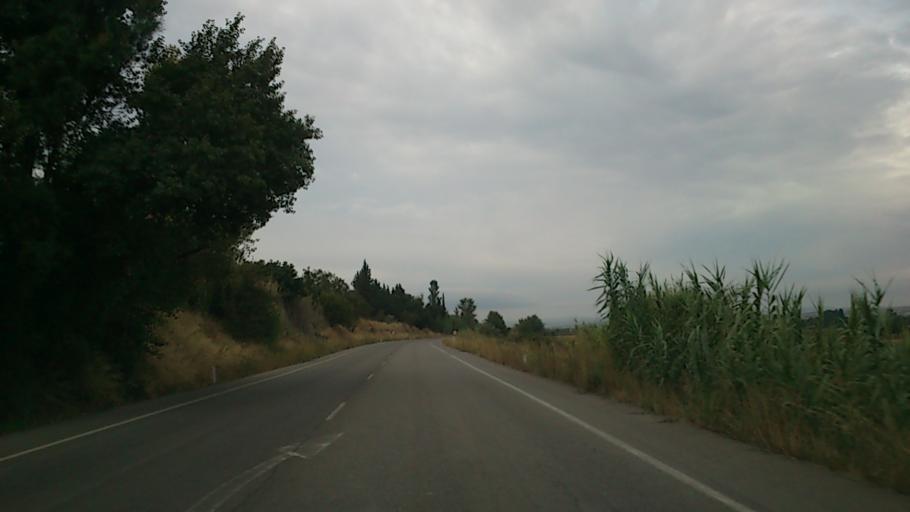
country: ES
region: Aragon
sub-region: Provincia de Zaragoza
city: Villanueva de Gallego
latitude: 41.7706
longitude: -0.7928
